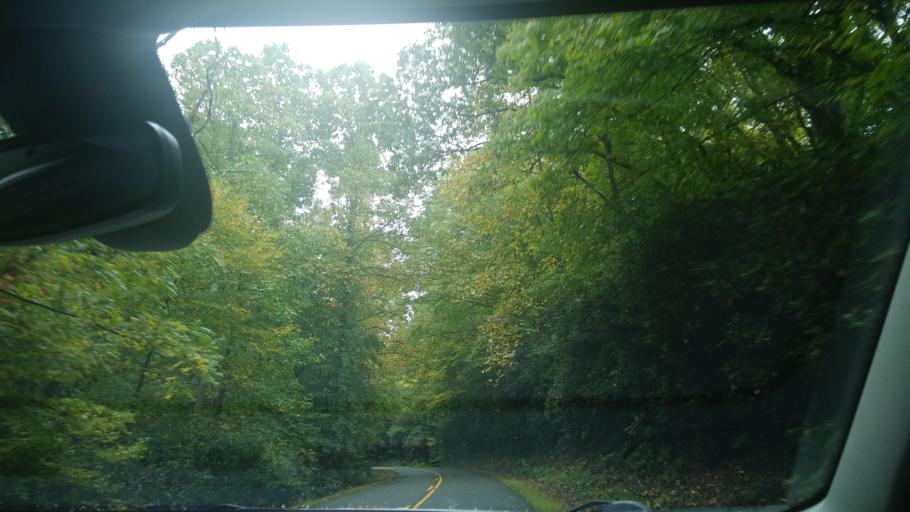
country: US
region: North Carolina
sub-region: Mitchell County
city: Spruce Pine
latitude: 35.8786
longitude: -82.0035
